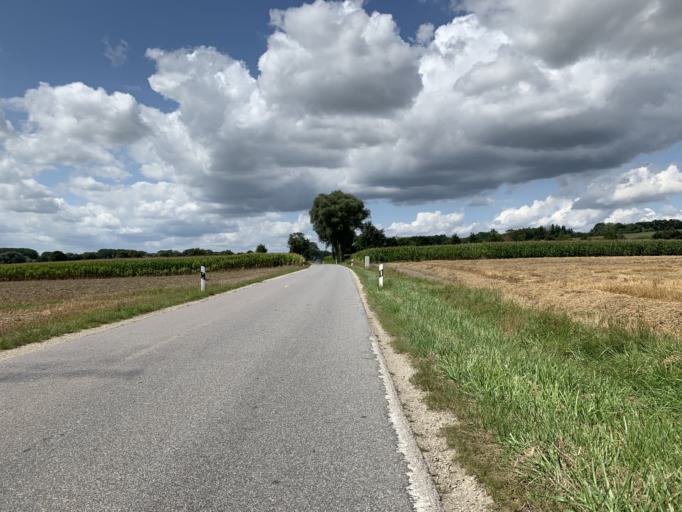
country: DE
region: Bavaria
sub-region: Upper Bavaria
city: Zolling
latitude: 48.4525
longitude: 11.7618
